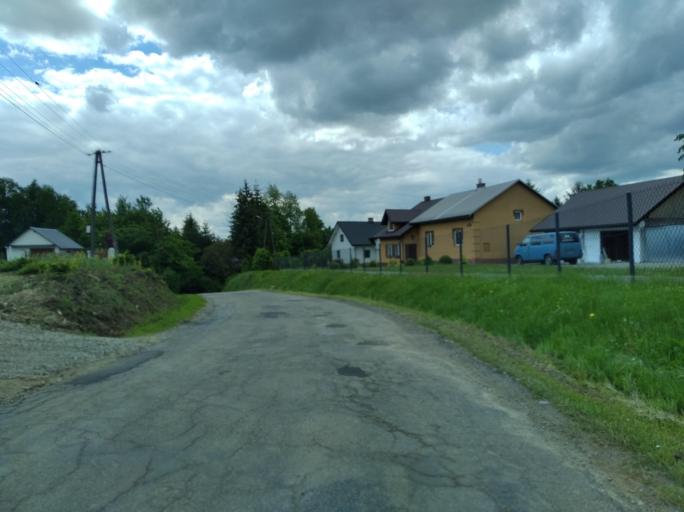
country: PL
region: Subcarpathian Voivodeship
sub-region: Powiat brzozowski
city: Jasionow
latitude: 49.6624
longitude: 21.9746
